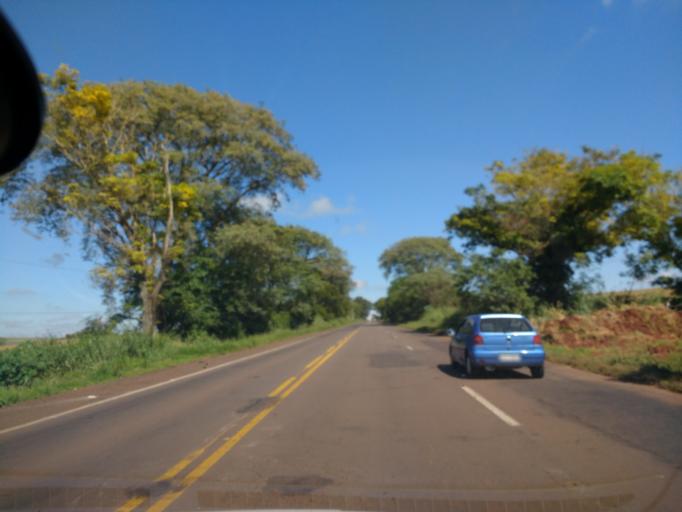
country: BR
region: Parana
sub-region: Terra Boa
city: Terra Boa
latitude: -23.6169
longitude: -52.4331
